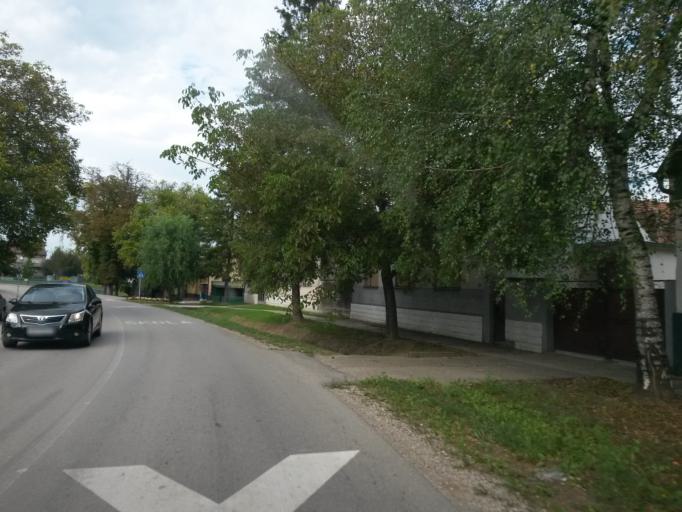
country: HR
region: Vukovarsko-Srijemska
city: Andrijasevci
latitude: 45.2261
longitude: 18.7414
